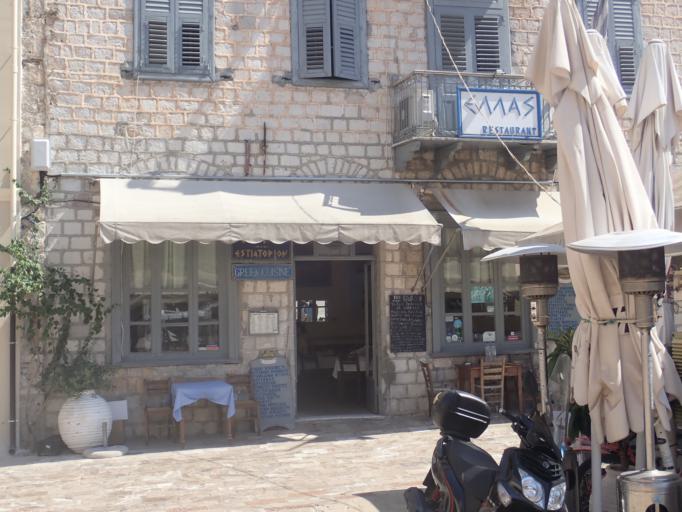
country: GR
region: Peloponnese
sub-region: Nomos Argolidos
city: Nafplio
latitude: 37.5661
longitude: 22.7971
